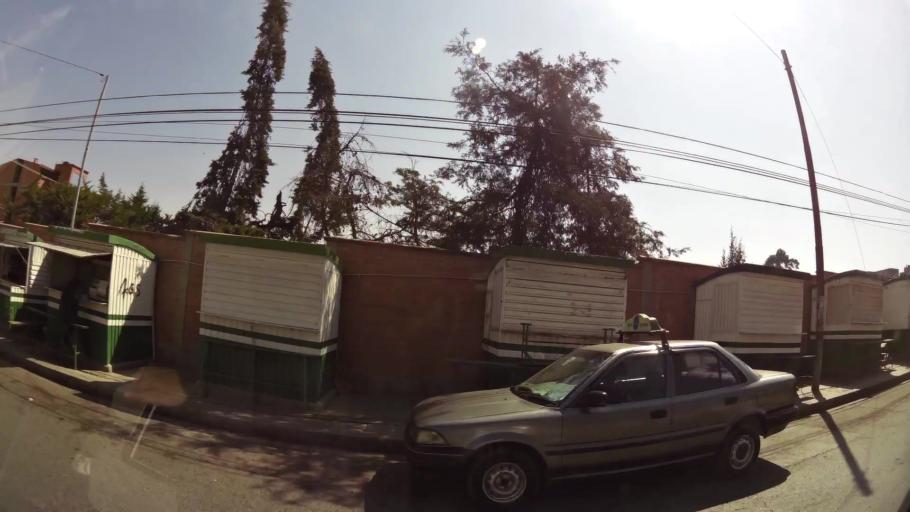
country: BO
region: La Paz
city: La Paz
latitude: -16.5453
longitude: -68.0640
